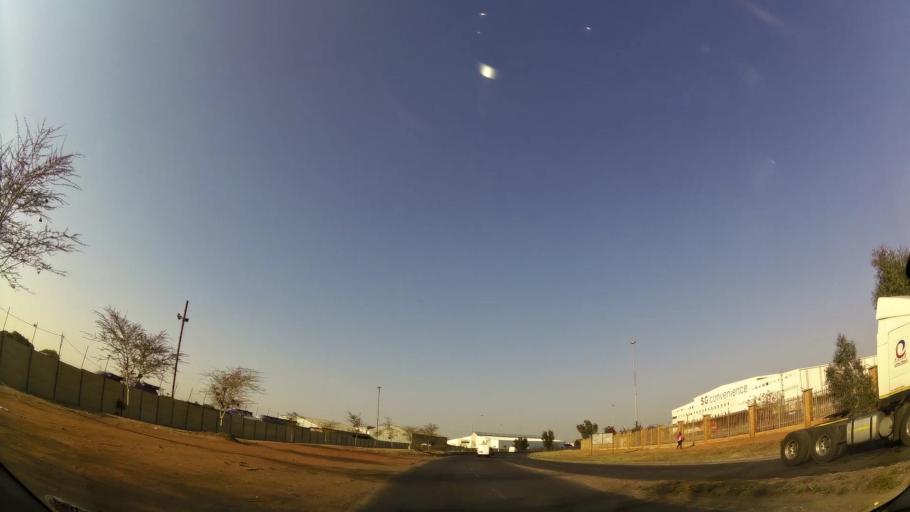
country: ZA
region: Gauteng
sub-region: City of Johannesburg Metropolitan Municipality
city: Modderfontein
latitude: -26.1523
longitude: 28.2024
